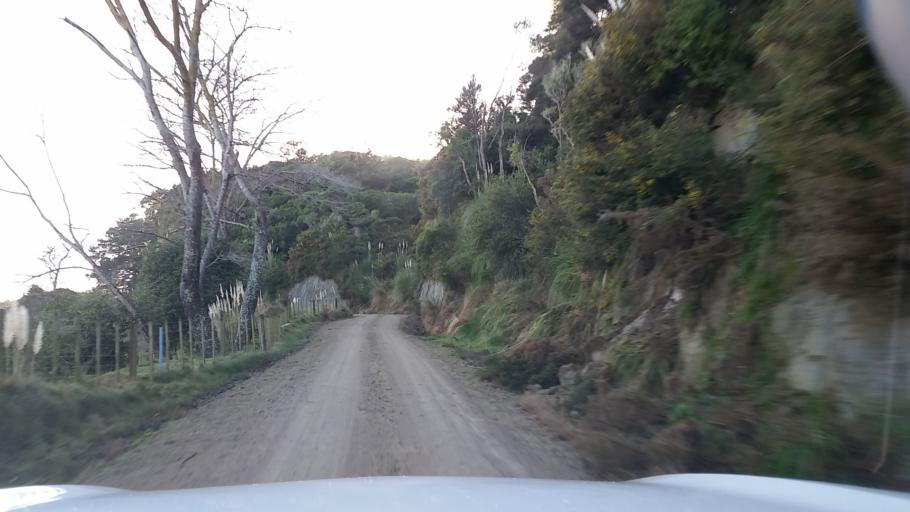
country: NZ
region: Taranaki
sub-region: South Taranaki District
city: Patea
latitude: -39.7588
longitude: 174.7380
